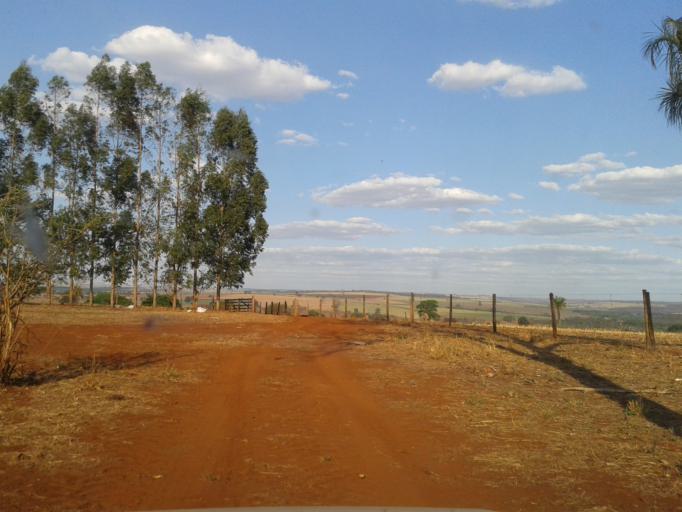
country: BR
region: Minas Gerais
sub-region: Capinopolis
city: Capinopolis
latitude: -18.6843
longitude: -49.3831
